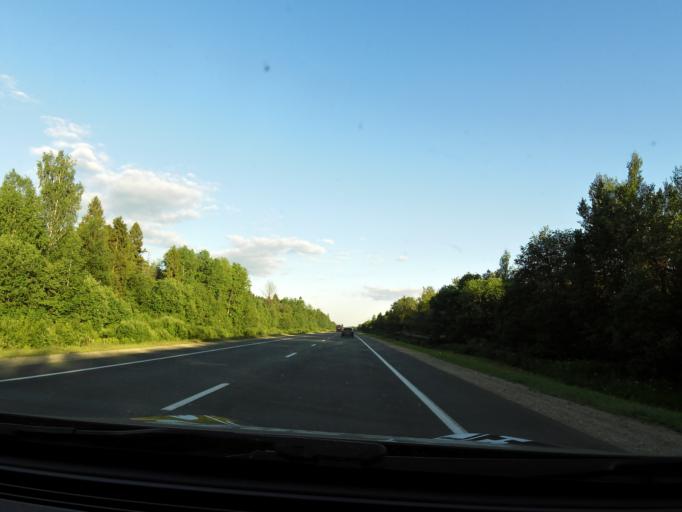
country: RU
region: Vologda
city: Vologda
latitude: 59.1019
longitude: 39.9905
